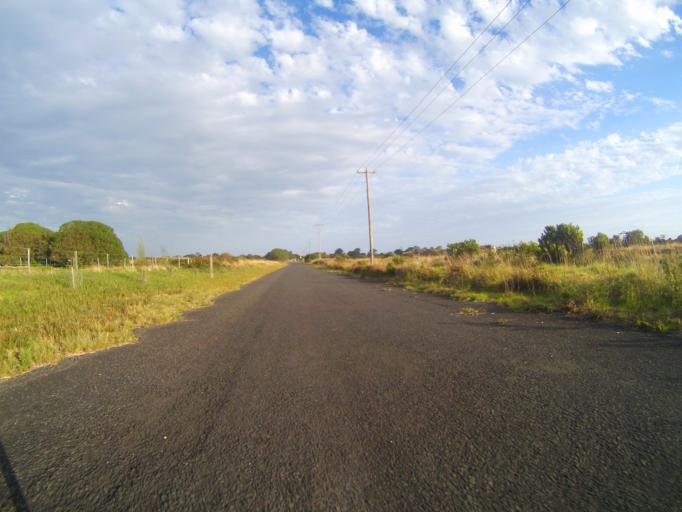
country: AU
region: Victoria
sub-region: Queenscliffe
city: Queenscliff
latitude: -38.2613
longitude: 144.6161
